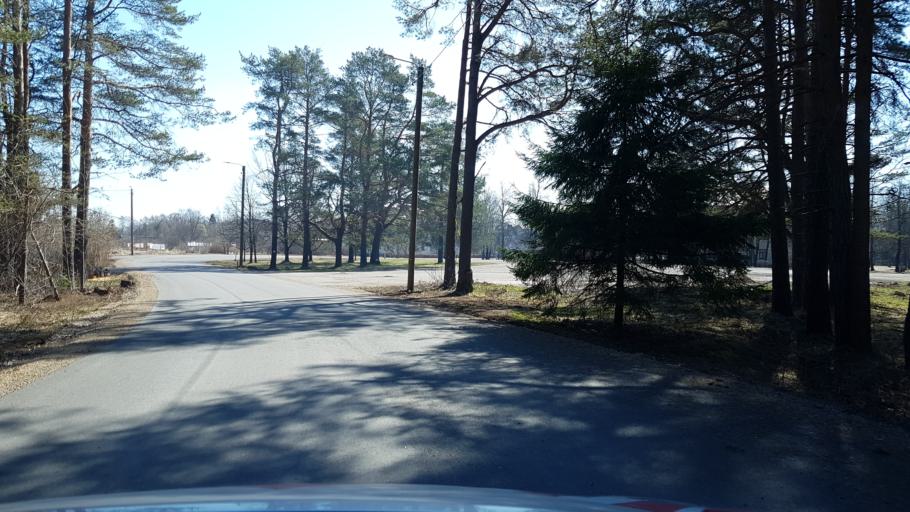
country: EE
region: Ida-Virumaa
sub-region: Kohtla-Nomme vald
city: Kohtla-Nomme
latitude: 59.3583
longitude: 27.1890
